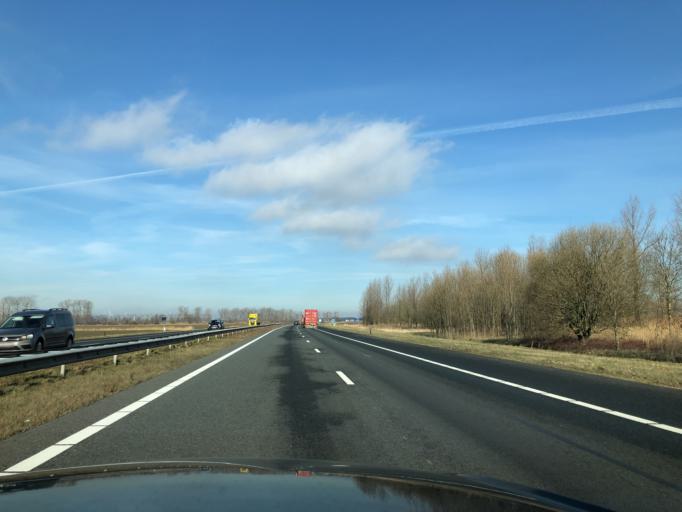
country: NL
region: North Brabant
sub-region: Gemeente Woensdrecht
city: Woensdrecht
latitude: 51.4088
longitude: 4.2829
